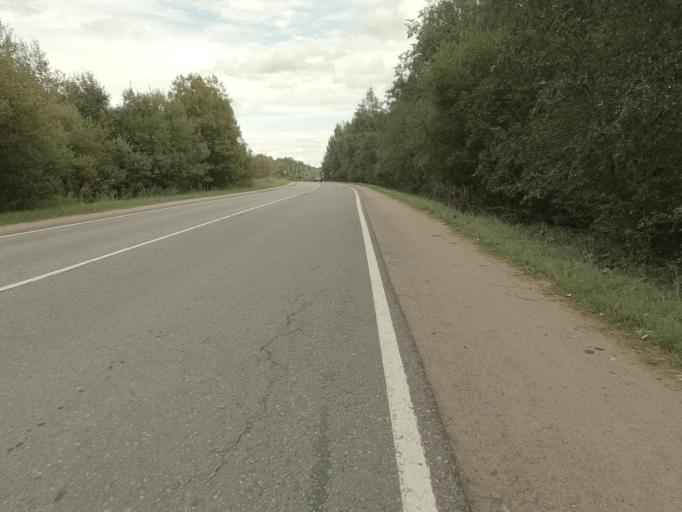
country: RU
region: Leningrad
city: Mga
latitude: 59.7625
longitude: 30.9906
